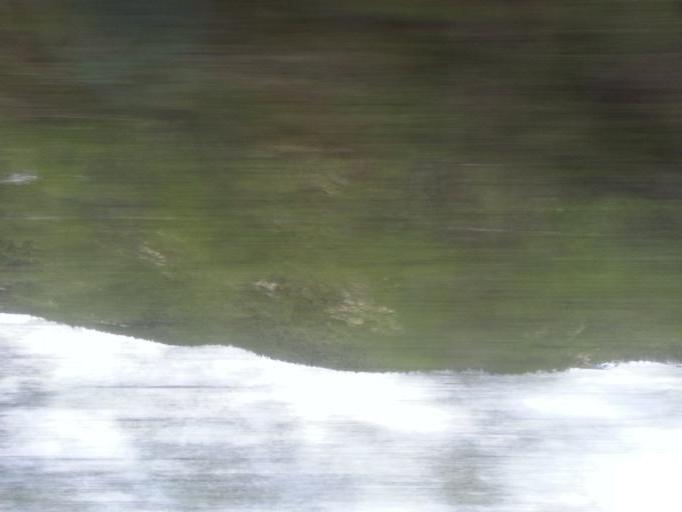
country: NO
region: Sor-Trondelag
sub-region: Oppdal
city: Oppdal
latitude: 62.2951
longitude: 9.5918
